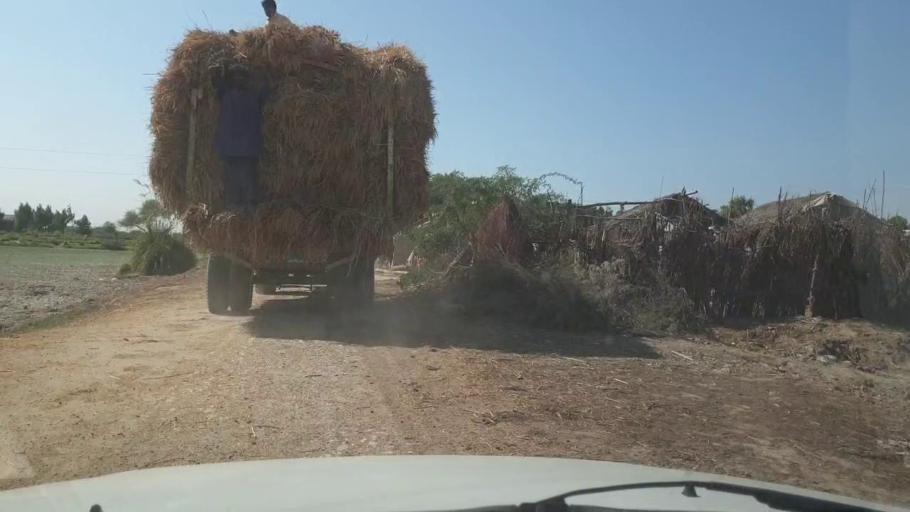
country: PK
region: Sindh
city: Mirpur Sakro
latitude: 24.4112
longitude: 67.7305
